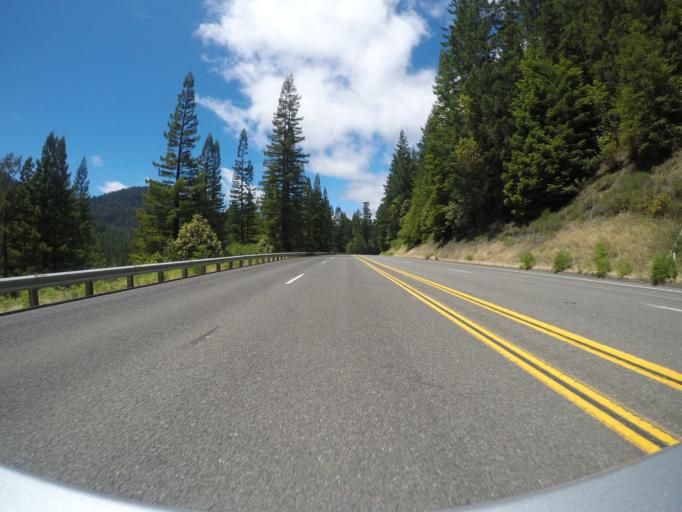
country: US
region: California
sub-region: Humboldt County
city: Redway
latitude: 40.2742
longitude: -123.8806
